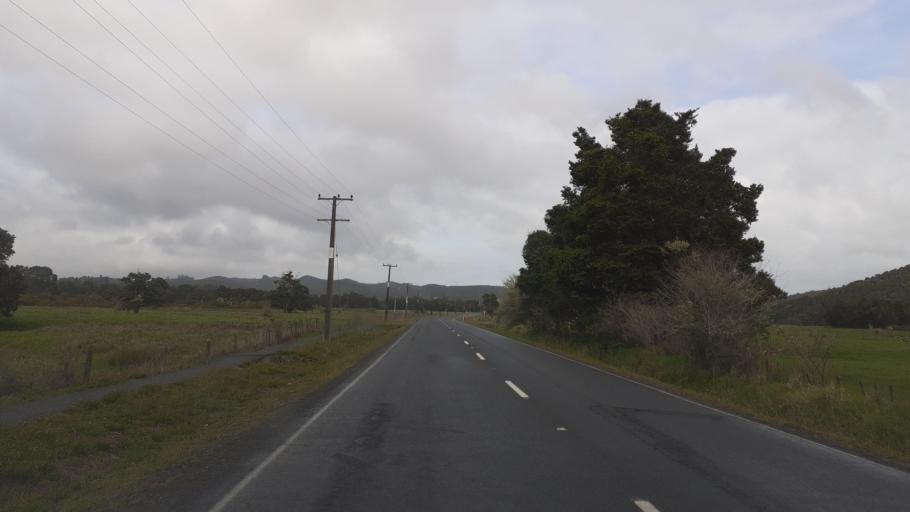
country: NZ
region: Northland
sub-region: Far North District
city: Moerewa
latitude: -35.3991
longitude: 173.9934
